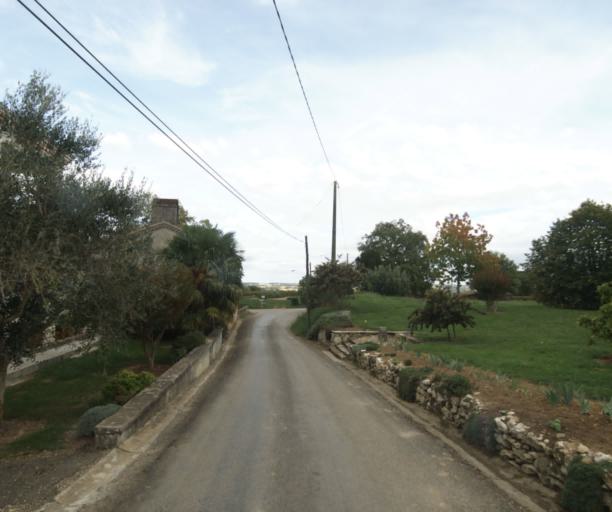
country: FR
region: Midi-Pyrenees
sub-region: Departement du Gers
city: Gondrin
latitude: 43.8721
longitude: 0.2487
